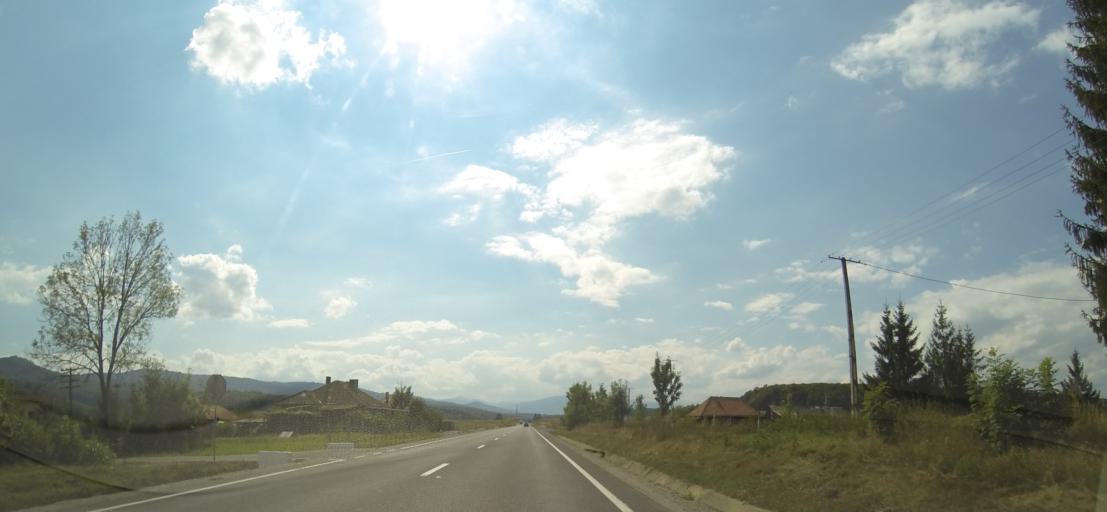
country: RO
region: Brasov
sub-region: Comuna Sinca Noua
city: Sinca Noua
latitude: 45.7506
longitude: 25.3095
